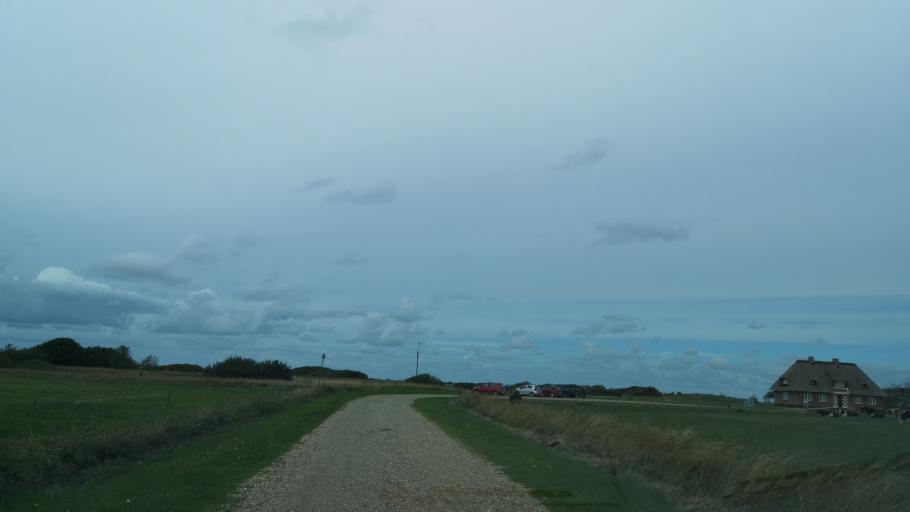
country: DK
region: Central Jutland
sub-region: Ringkobing-Skjern Kommune
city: Hvide Sande
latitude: 55.8947
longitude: 8.2138
